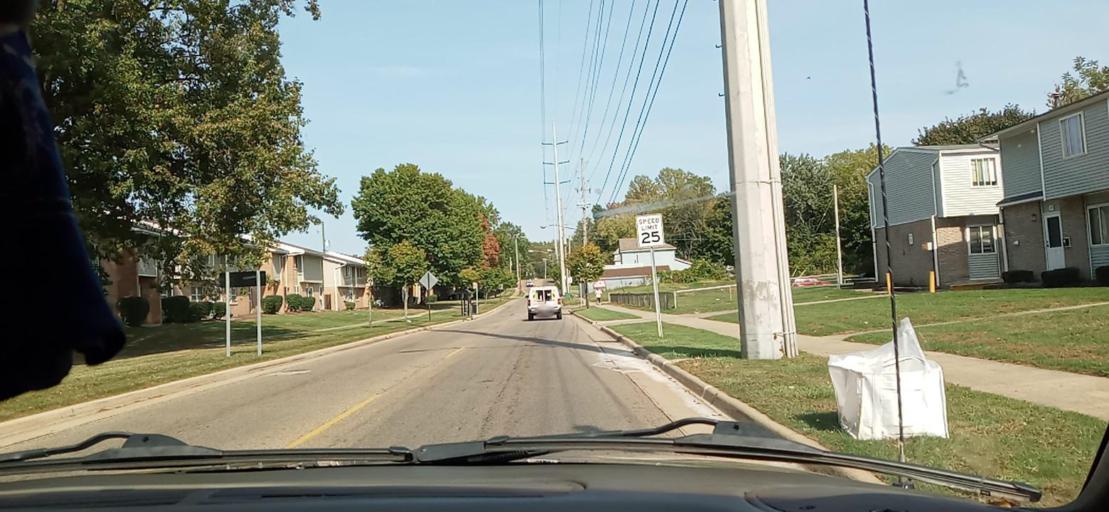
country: US
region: Ohio
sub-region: Summit County
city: Akron
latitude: 41.0544
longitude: -81.5412
